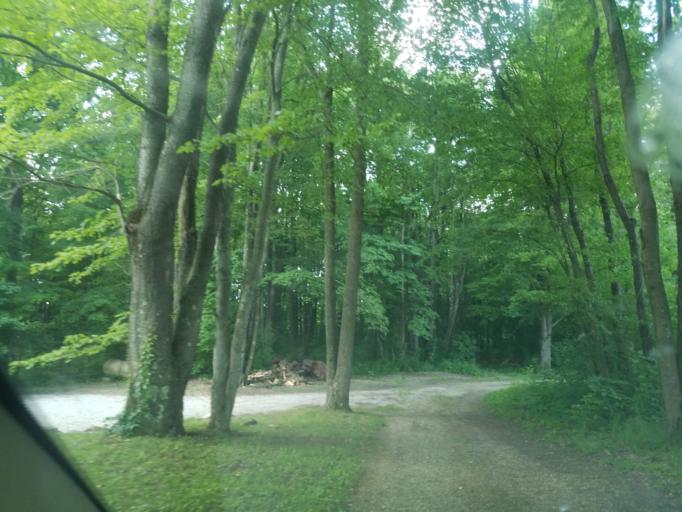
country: US
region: Ohio
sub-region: Sandusky County
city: Bellville
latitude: 40.5809
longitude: -82.5797
